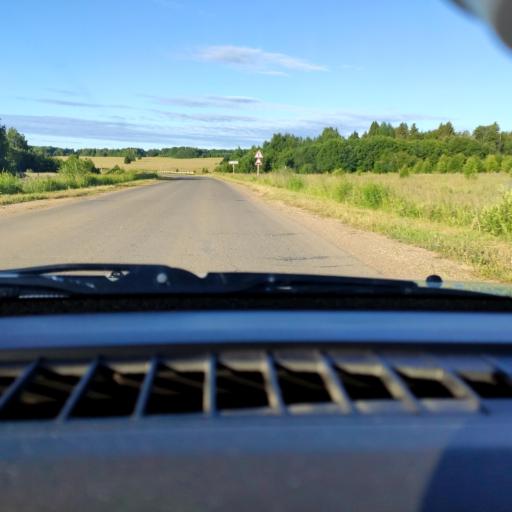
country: RU
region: Perm
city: Uinskoye
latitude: 57.0830
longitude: 56.5552
